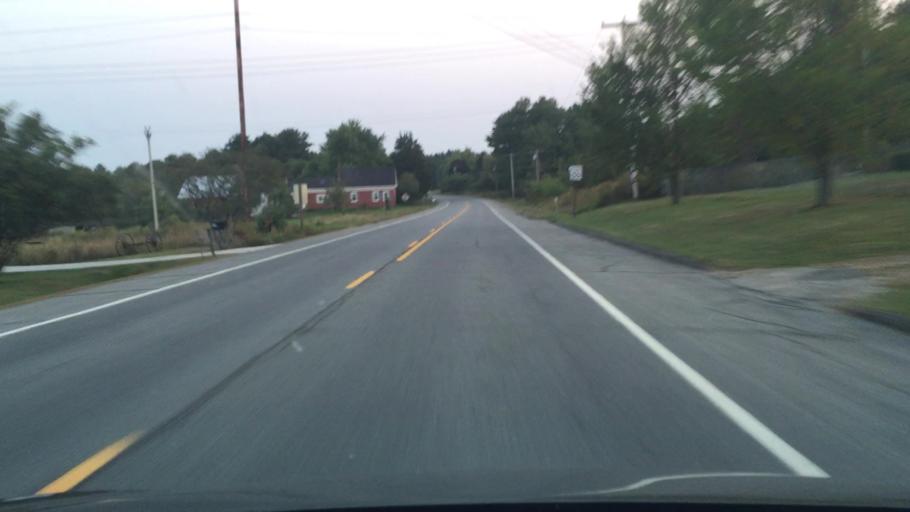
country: US
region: Maine
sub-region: Waldo County
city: Frankfort
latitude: 44.5505
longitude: -68.8643
